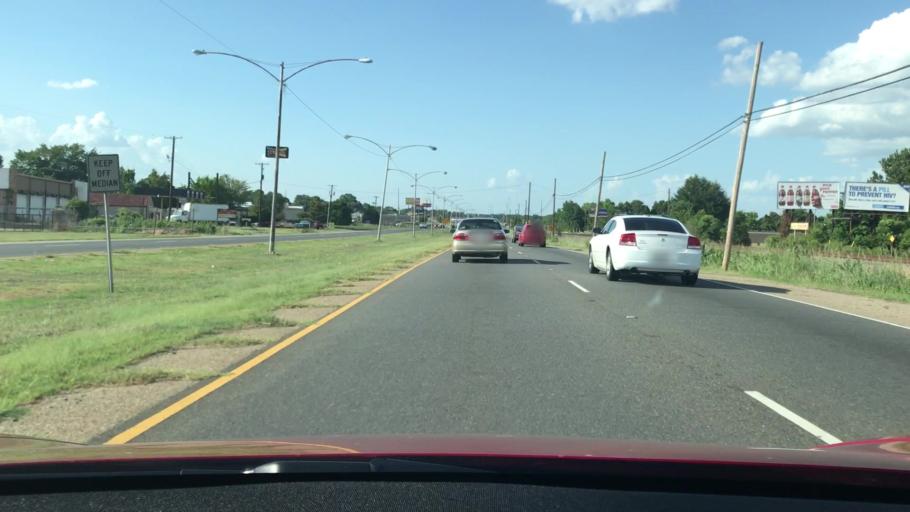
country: US
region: Louisiana
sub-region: Bossier Parish
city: Bossier City
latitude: 32.4370
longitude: -93.7825
